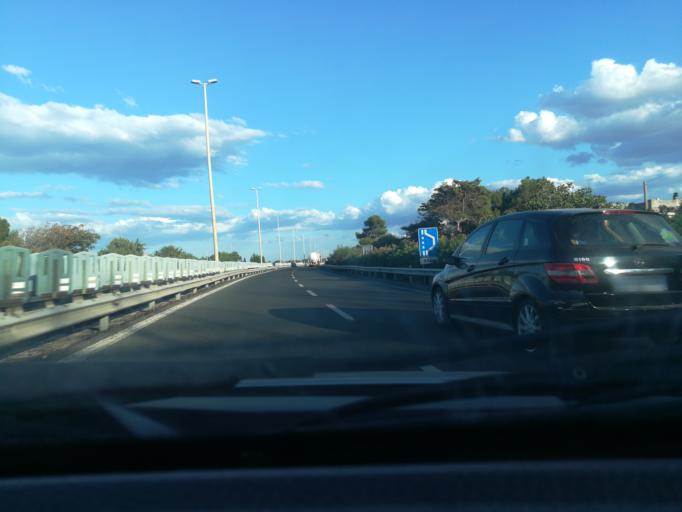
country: IT
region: Apulia
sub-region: Provincia di Bari
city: Mola di Bari
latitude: 41.0774
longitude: 17.0484
